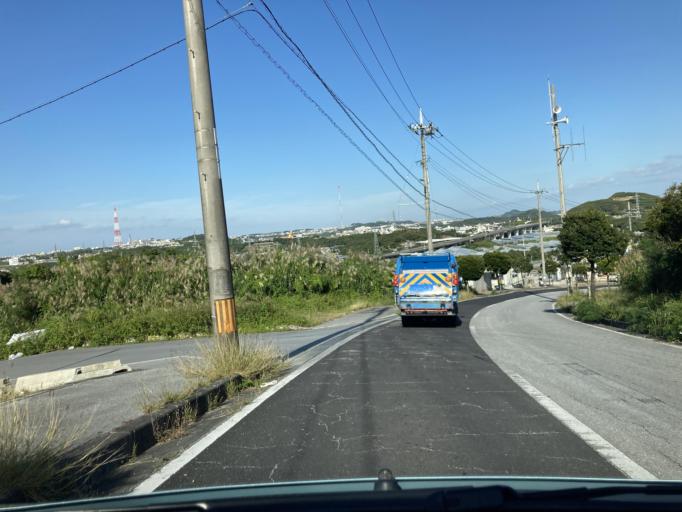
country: JP
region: Okinawa
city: Tomigusuku
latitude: 26.1692
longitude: 127.6983
